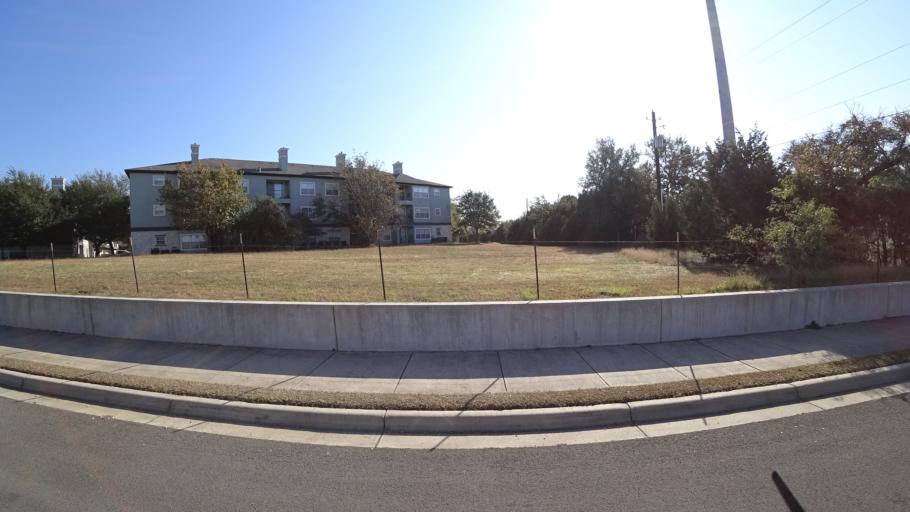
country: US
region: Texas
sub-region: Williamson County
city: Anderson Mill
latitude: 30.3901
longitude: -97.8432
